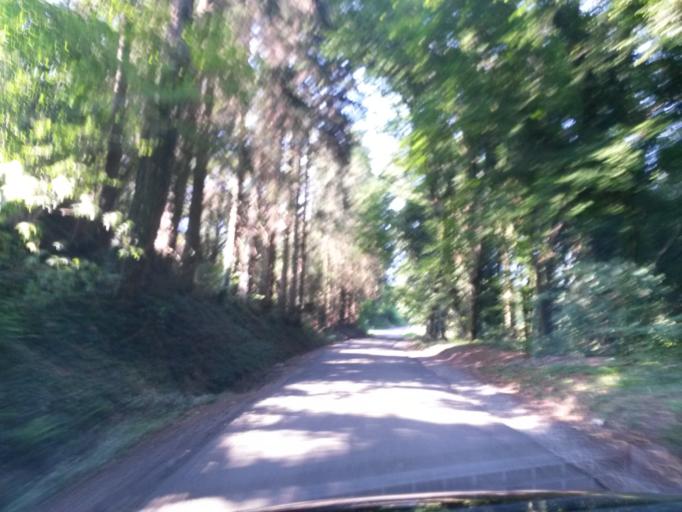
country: DE
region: North Rhine-Westphalia
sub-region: Regierungsbezirk Koln
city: Rosrath
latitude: 50.8772
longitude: 7.2090
